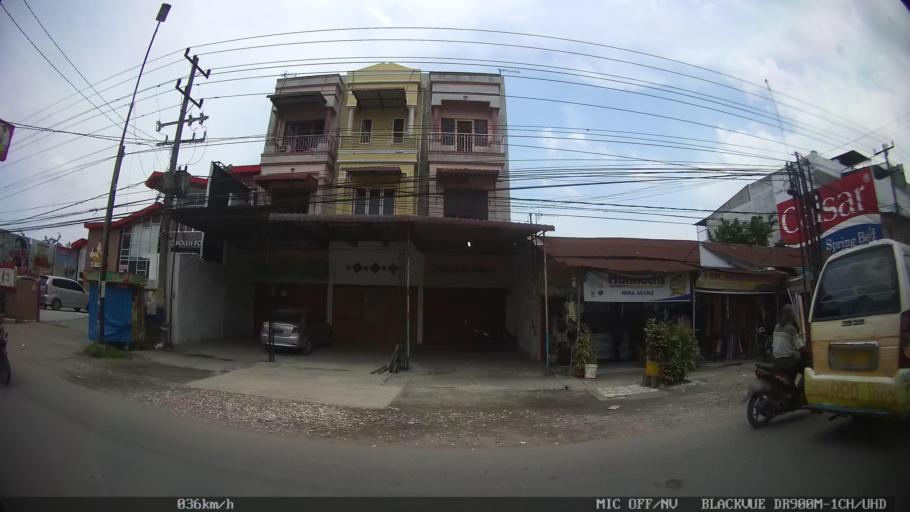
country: ID
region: North Sumatra
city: Labuhan Deli
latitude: 3.6982
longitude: 98.6560
